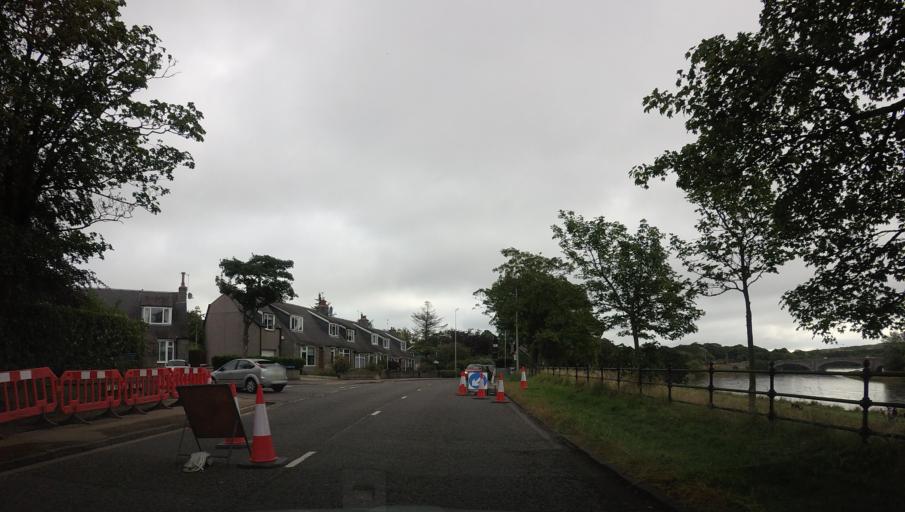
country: GB
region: Scotland
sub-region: Aberdeen City
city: Aberdeen
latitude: 57.1288
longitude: -2.1148
